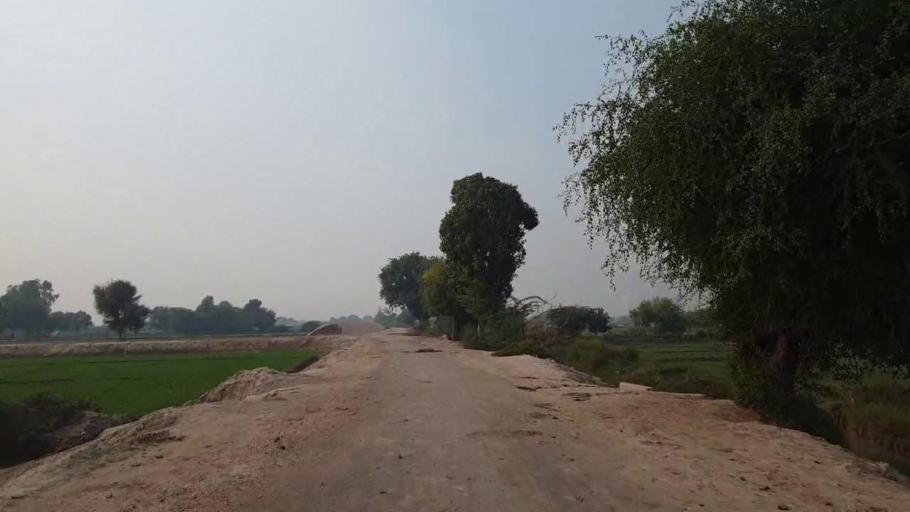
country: PK
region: Sindh
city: Bhan
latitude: 26.5419
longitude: 67.7133
